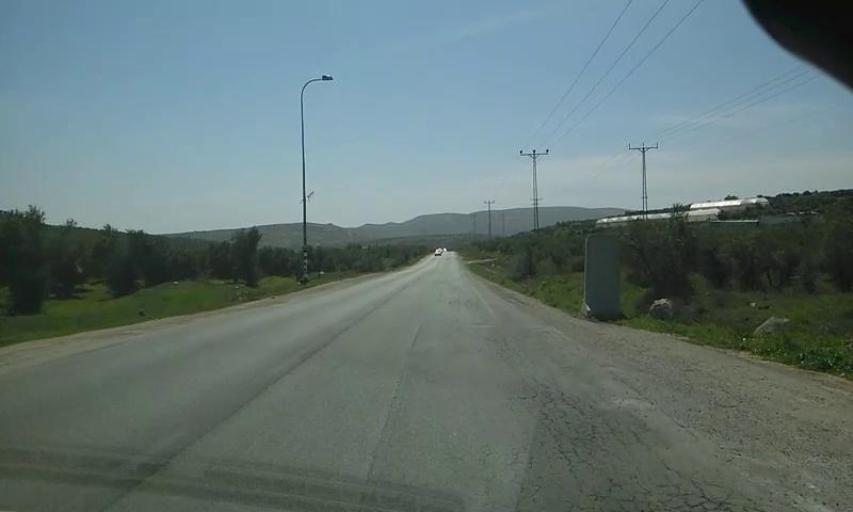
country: PS
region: West Bank
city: Marah Rabbah
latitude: 31.6381
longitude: 35.2026
